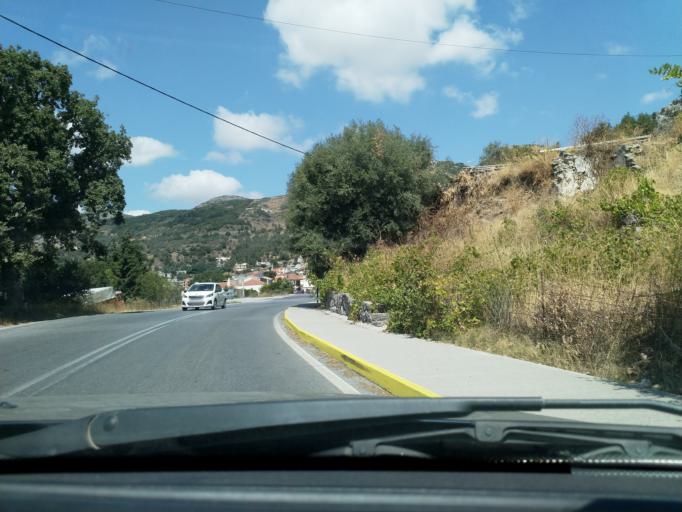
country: GR
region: Crete
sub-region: Nomos Rethymnis
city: Agia Foteini
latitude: 35.2139
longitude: 24.5354
